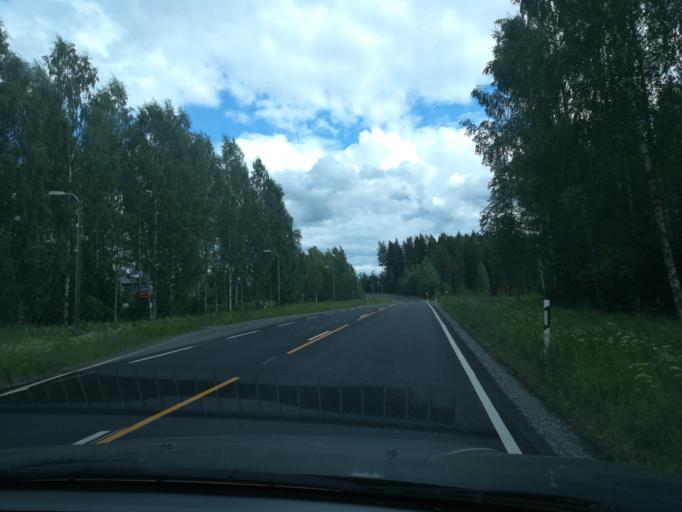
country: FI
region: Southern Savonia
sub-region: Mikkeli
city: Mikkeli
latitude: 61.6579
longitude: 27.1202
